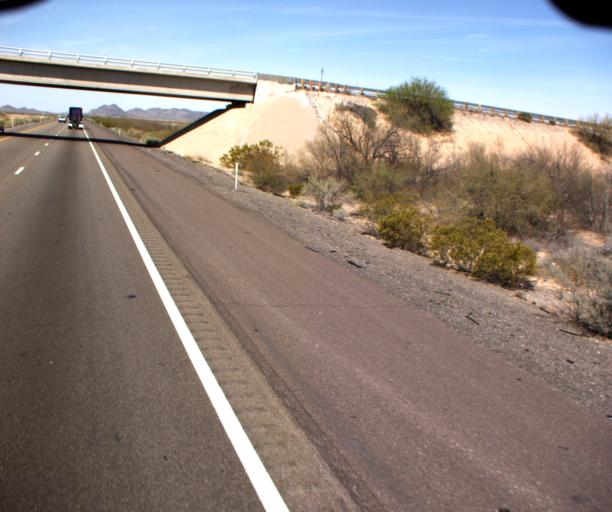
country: US
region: Arizona
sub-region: La Paz County
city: Salome
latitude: 33.5953
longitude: -113.5255
